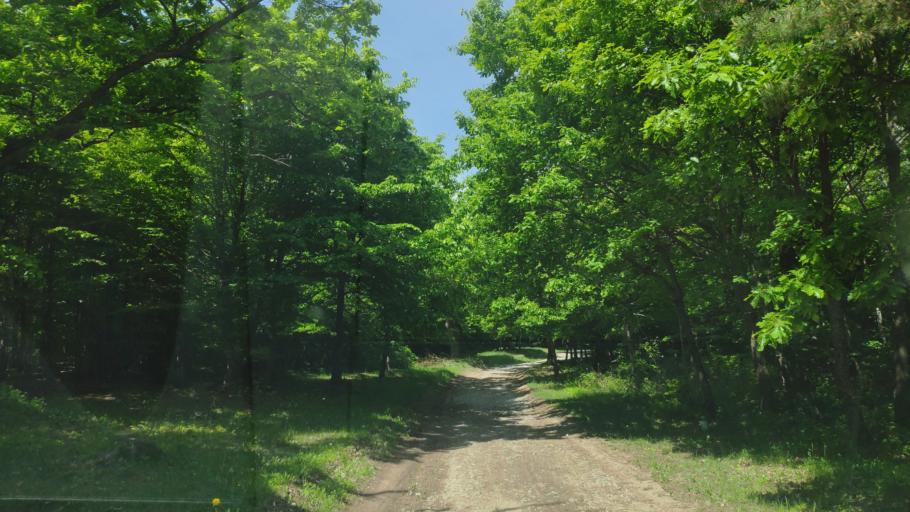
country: SK
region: Kosicky
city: Secovce
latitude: 48.7014
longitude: 21.5862
